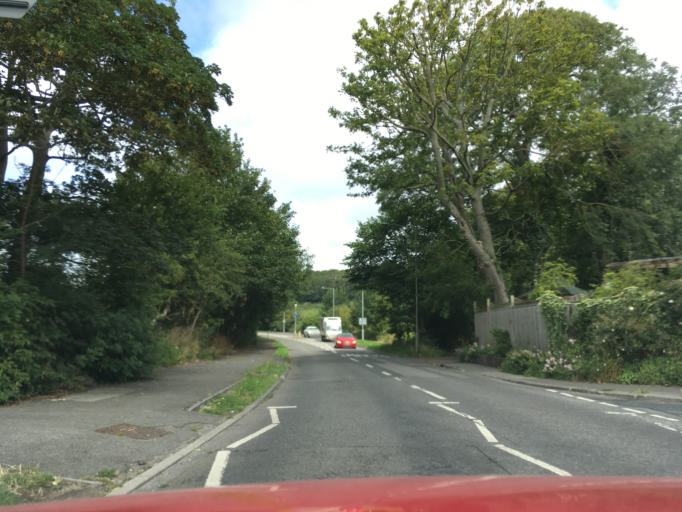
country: GB
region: England
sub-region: Brighton and Hove
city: Rottingdean
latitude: 50.8239
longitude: -0.0678
